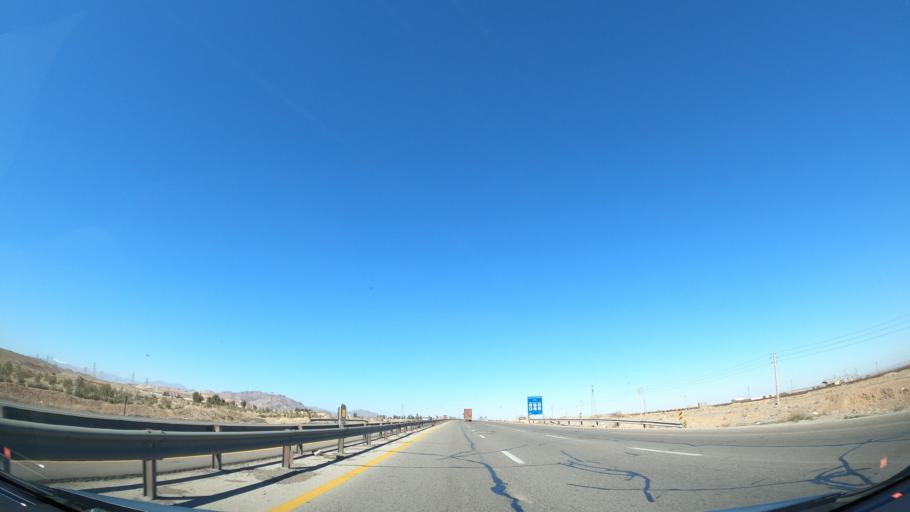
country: IR
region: Isfahan
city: Kashan
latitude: 33.9880
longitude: 51.3340
